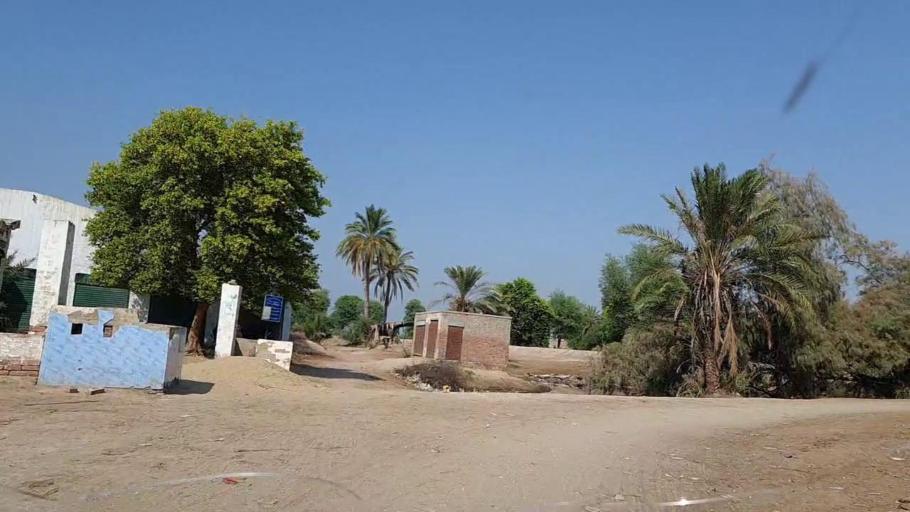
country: PK
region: Sindh
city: Khanpur
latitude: 27.7360
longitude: 69.3506
